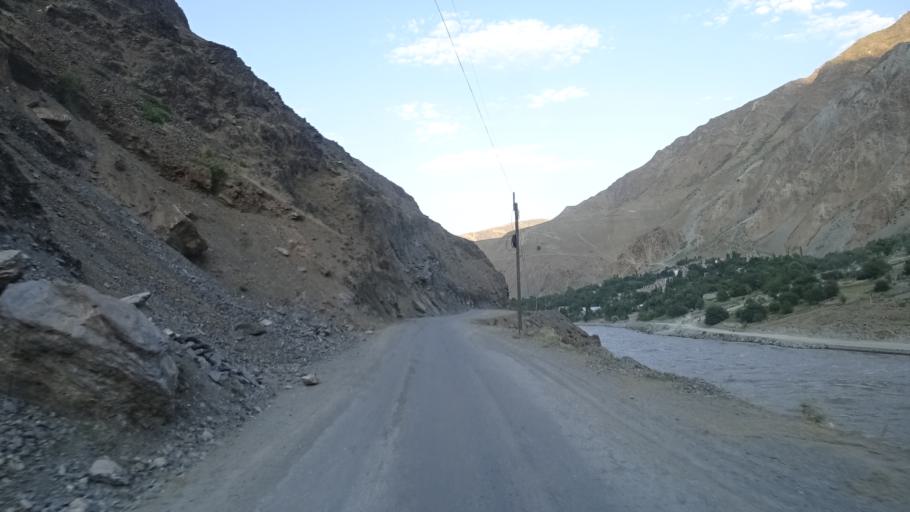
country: AF
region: Badakhshan
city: Nusay
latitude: 38.4453
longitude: 70.8086
